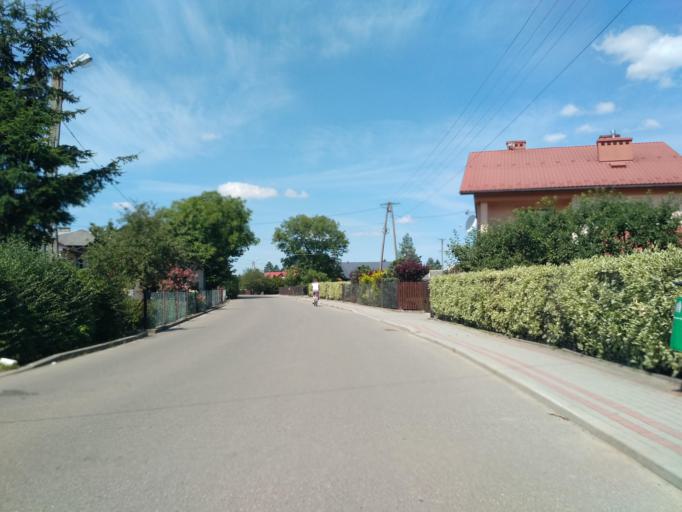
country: PL
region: Subcarpathian Voivodeship
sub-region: Powiat krosnienski
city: Kroscienko Wyzne
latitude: 49.6555
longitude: 21.8377
